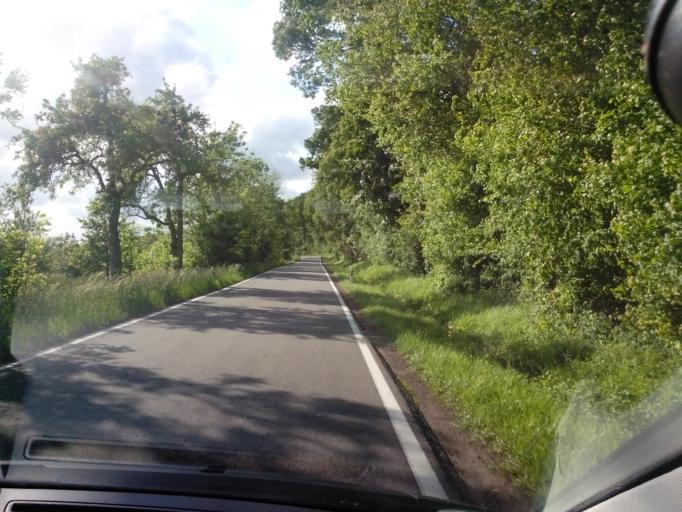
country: DE
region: Saarland
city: Rehlingen-Siersburg
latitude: 49.3760
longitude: 6.6253
